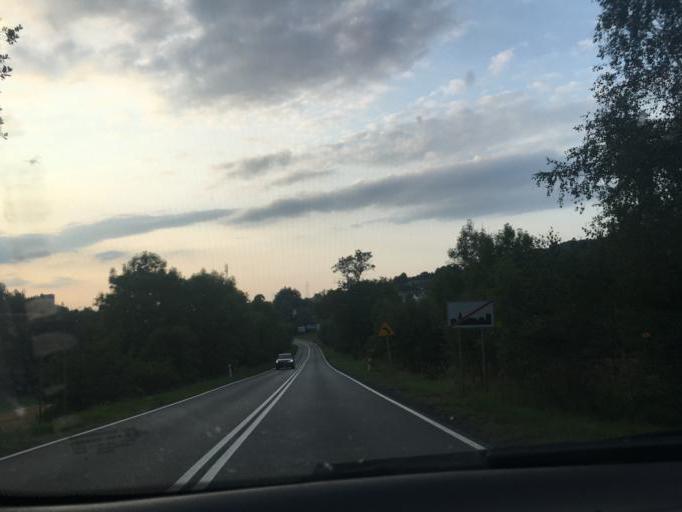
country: PL
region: Lower Silesian Voivodeship
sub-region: Powiat klodzki
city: Bozkow
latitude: 50.5337
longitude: 16.5806
